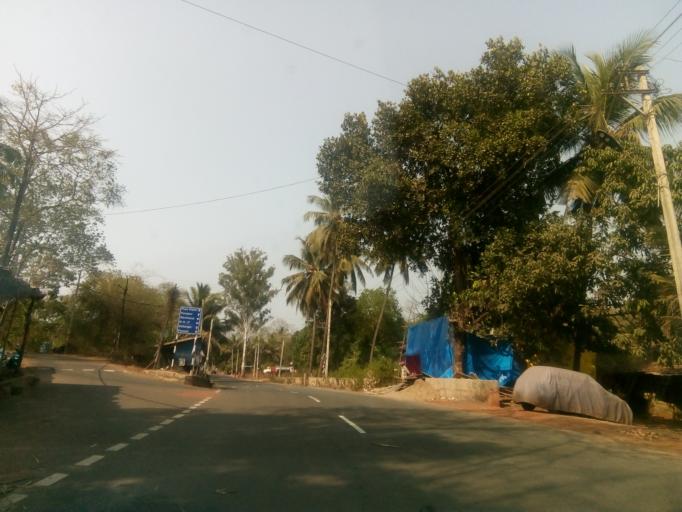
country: IN
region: Goa
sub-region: North Goa
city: Pernem
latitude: 15.7063
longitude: 73.8527
